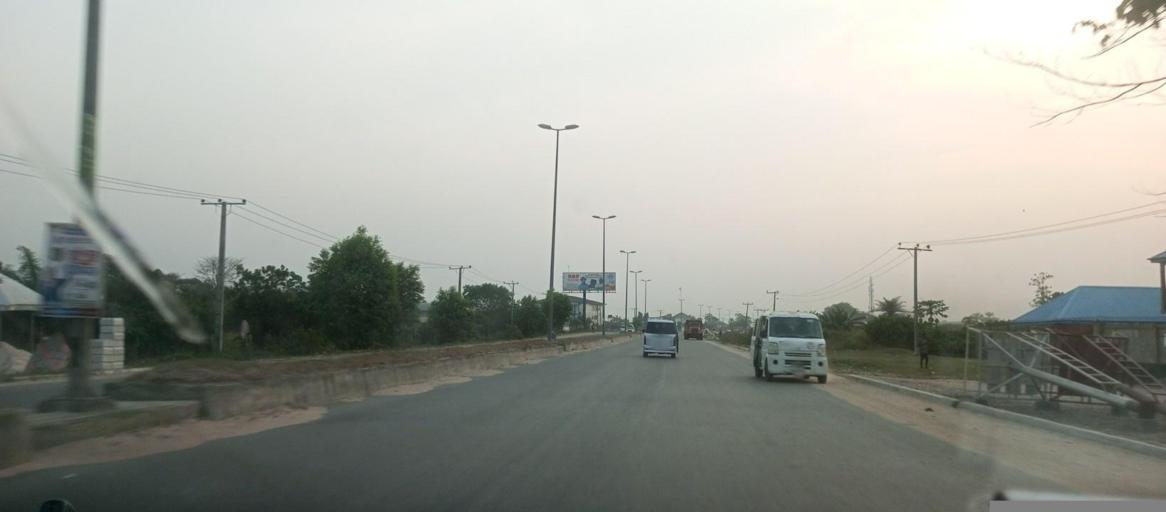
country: NG
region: Rivers
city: Emuoha
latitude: 4.9371
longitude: 7.0065
